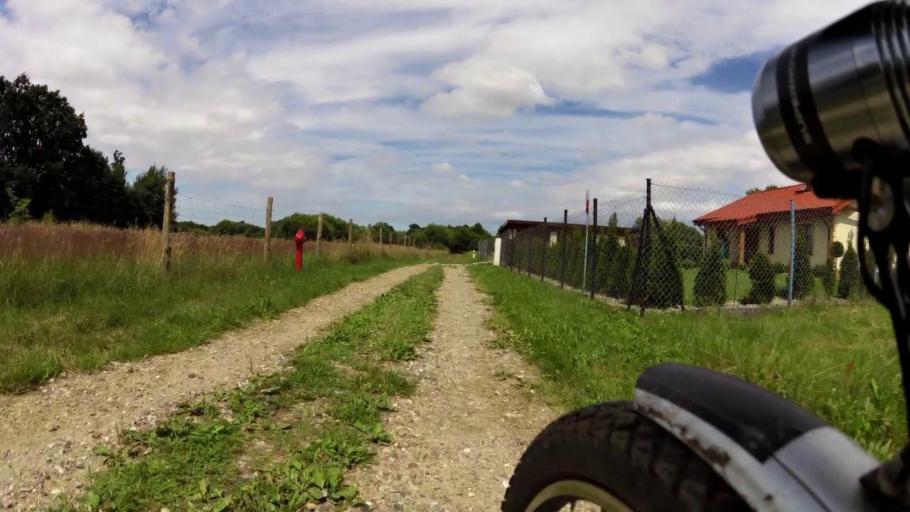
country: PL
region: West Pomeranian Voivodeship
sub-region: Powiat bialogardzki
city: Bialogard
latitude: 53.9817
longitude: 16.0022
